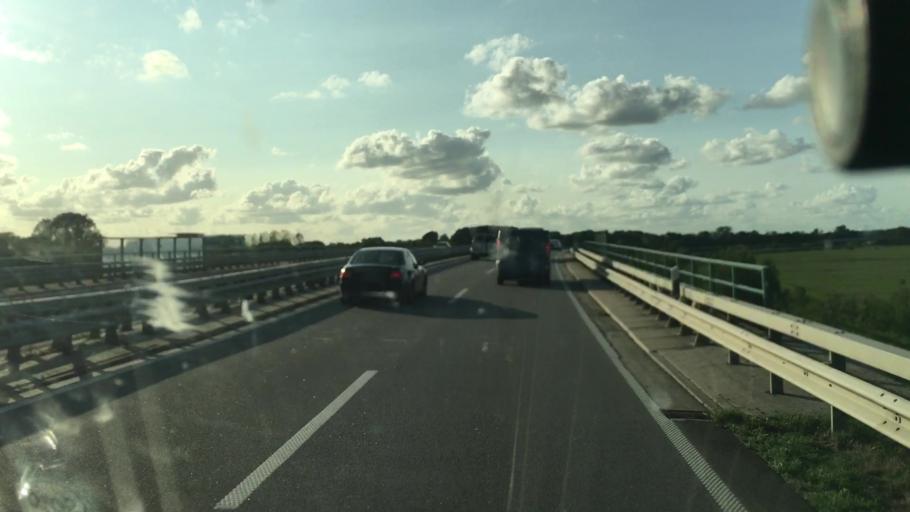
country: DE
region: Lower Saxony
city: Schortens
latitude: 53.5313
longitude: 7.9859
